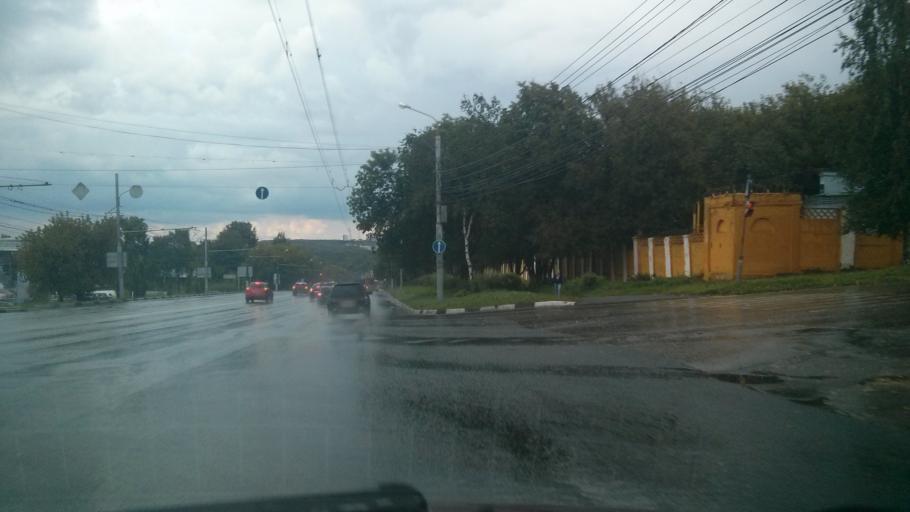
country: RU
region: Nizjnij Novgorod
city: Nizhniy Novgorod
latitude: 56.2461
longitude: 43.9659
